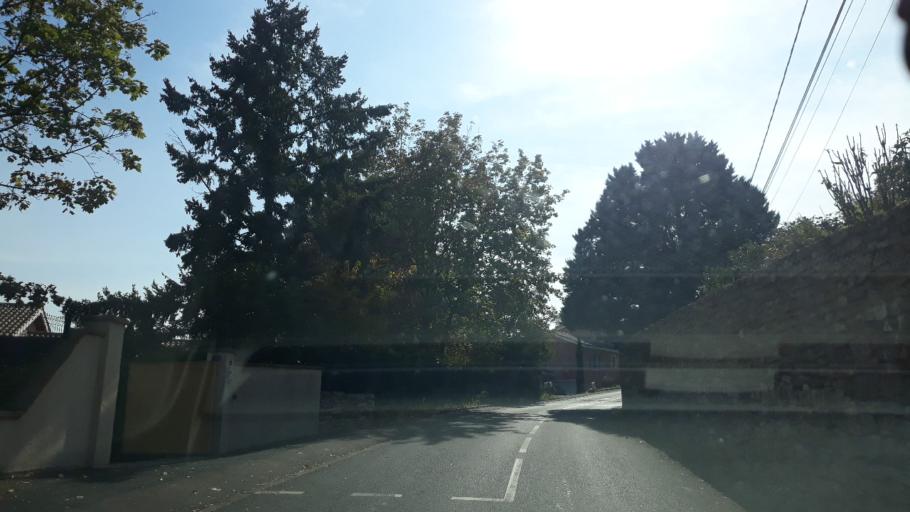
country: FR
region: Rhone-Alpes
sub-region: Departement du Rhone
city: Limas
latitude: 45.9713
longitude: 4.7084
